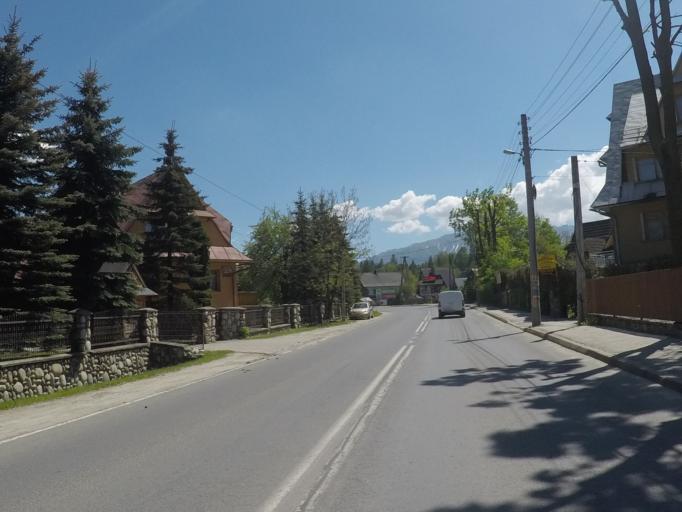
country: PL
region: Lesser Poland Voivodeship
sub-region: Powiat tatrzanski
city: Poronin
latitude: 49.3358
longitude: 20.0067
